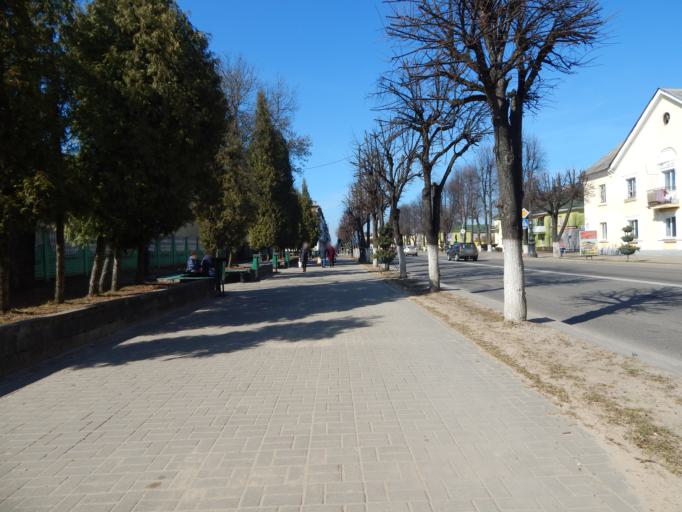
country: BY
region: Minsk
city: Horad Barysaw
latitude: 54.2224
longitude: 28.5196
